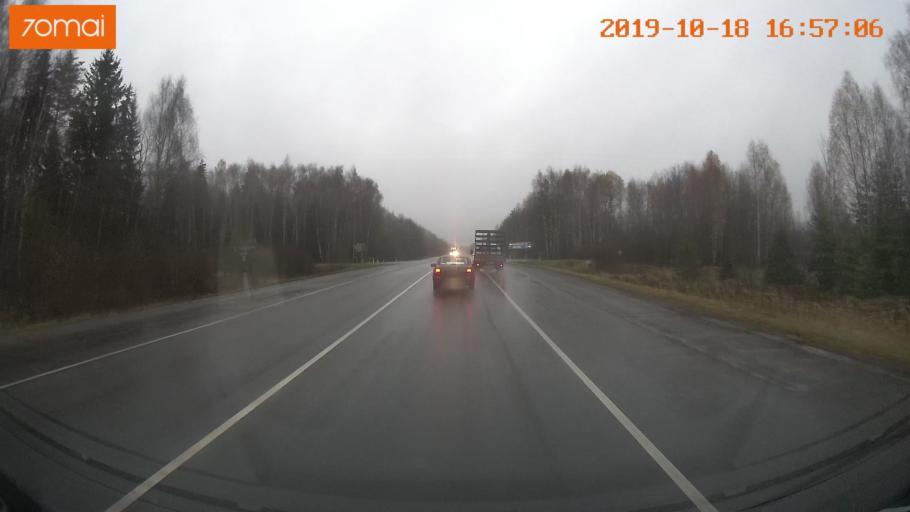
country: RU
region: Ivanovo
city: Novoye Leushino
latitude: 56.6633
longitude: 40.5924
